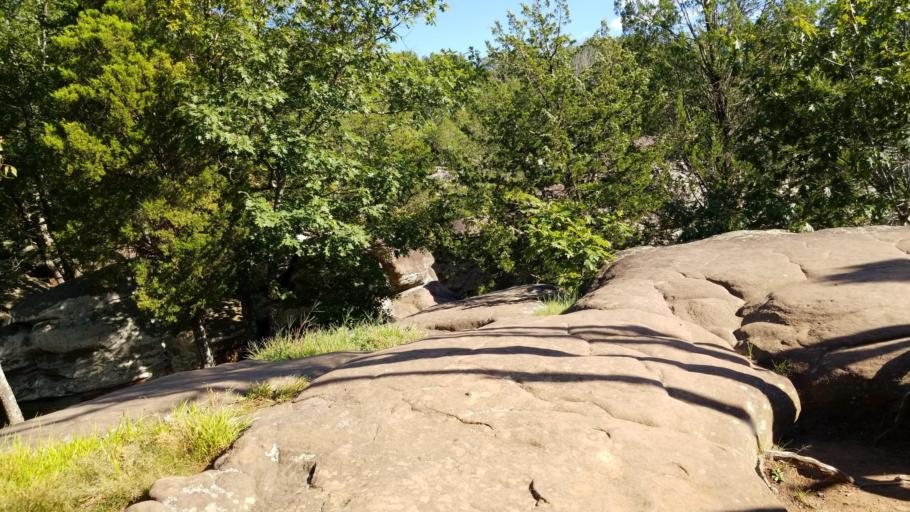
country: US
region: Illinois
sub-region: Hardin County
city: Elizabethtown
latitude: 37.6050
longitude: -88.3860
